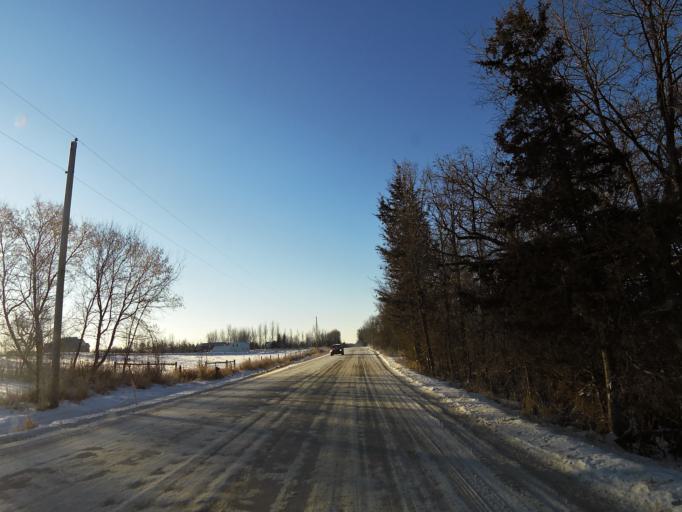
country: US
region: Minnesota
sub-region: Scott County
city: Jordan
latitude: 44.6456
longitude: -93.5161
